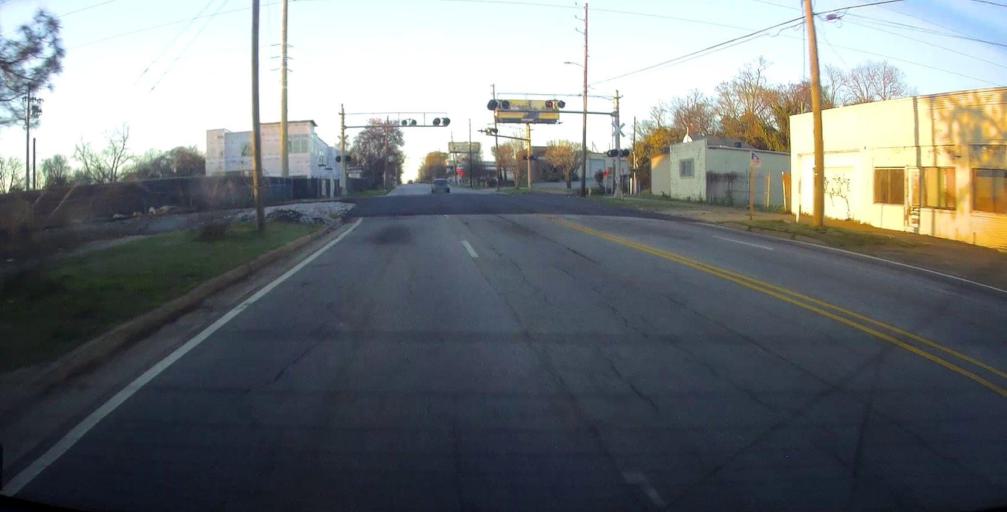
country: US
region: Alabama
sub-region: Russell County
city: Phenix City
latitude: 32.4826
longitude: -84.9903
